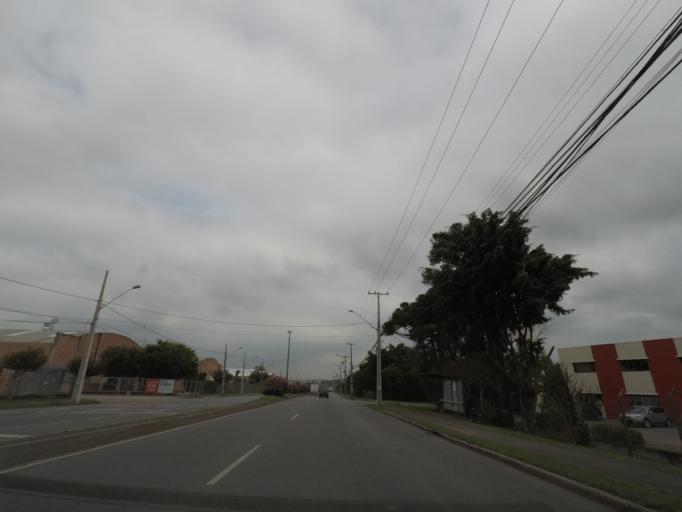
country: BR
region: Parana
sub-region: Curitiba
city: Curitiba
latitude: -25.5089
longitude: -49.3303
